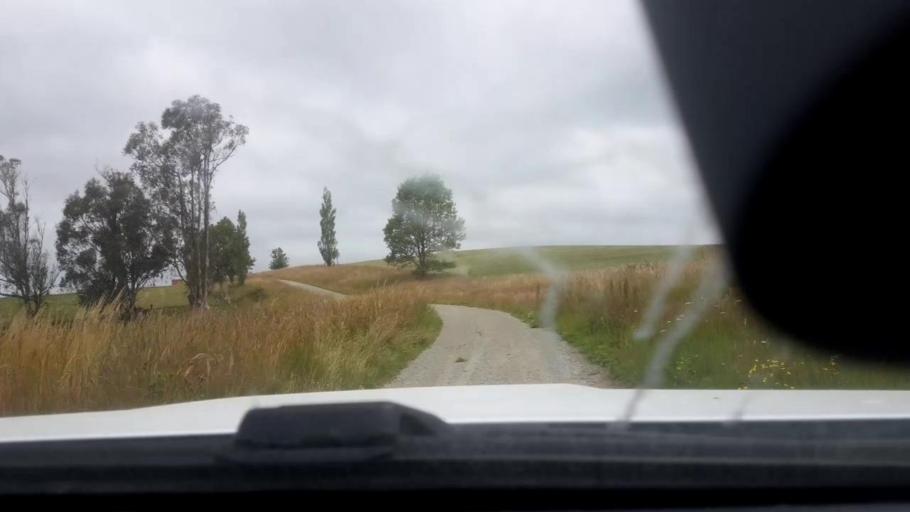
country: NZ
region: Canterbury
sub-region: Timaru District
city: Pleasant Point
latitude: -44.1963
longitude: 171.1880
